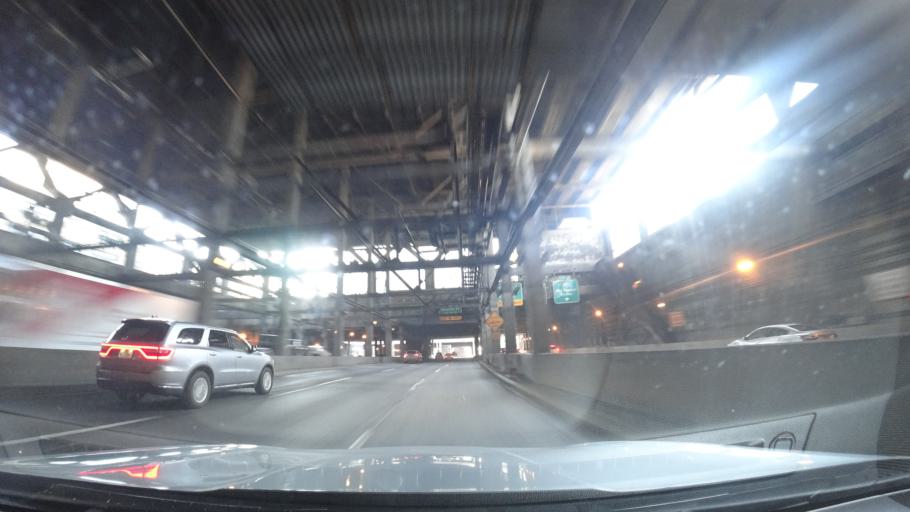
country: US
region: New York
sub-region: New York County
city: Inwood
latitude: 40.8485
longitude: -73.9372
